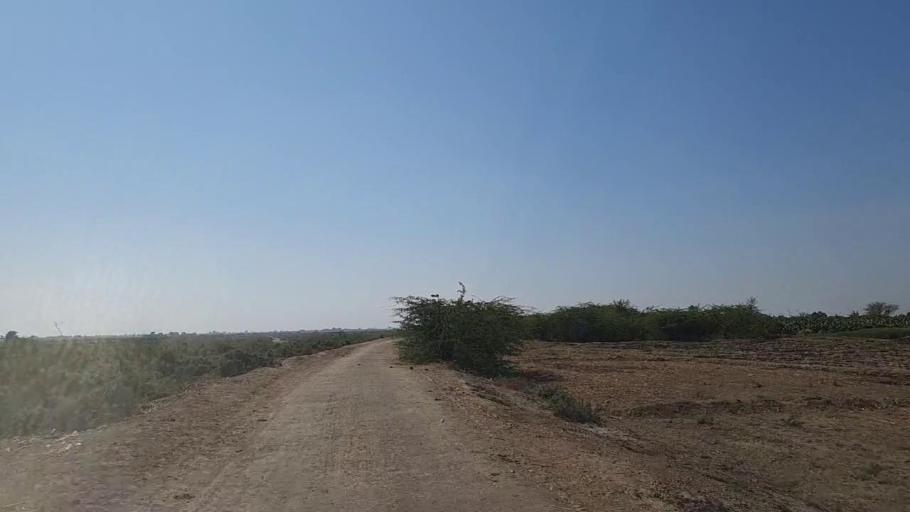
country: PK
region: Sindh
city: Pithoro
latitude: 25.4233
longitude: 69.3764
